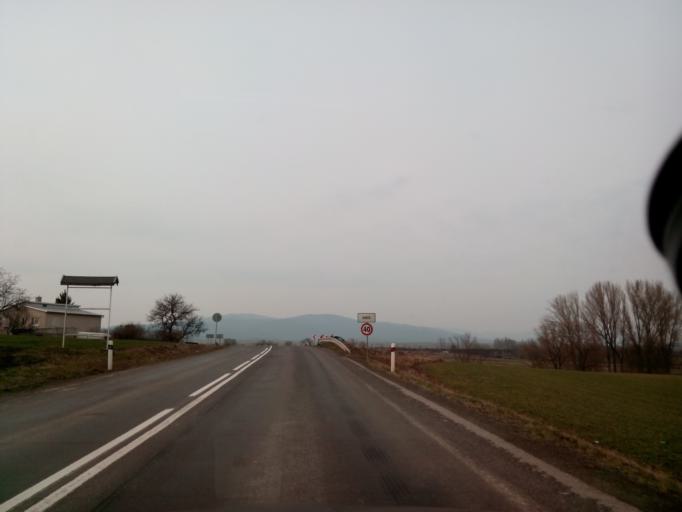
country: SK
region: Kosicky
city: Secovce
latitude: 48.6109
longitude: 21.6159
